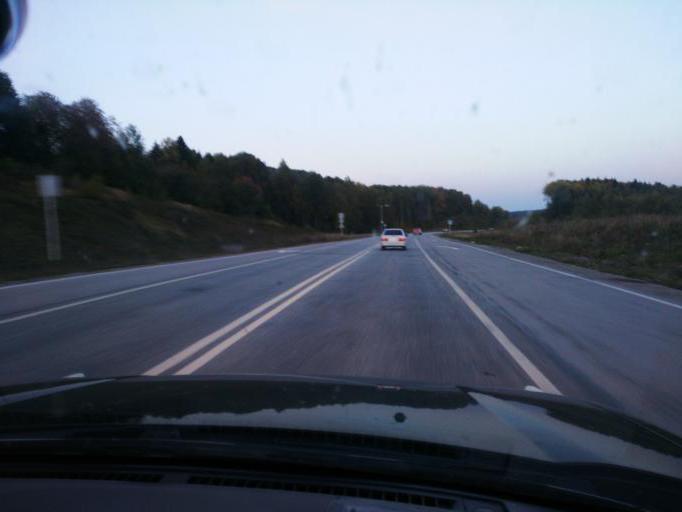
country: RU
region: Perm
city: Verkhnechusovskiye Gorodki
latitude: 58.2963
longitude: 56.8634
